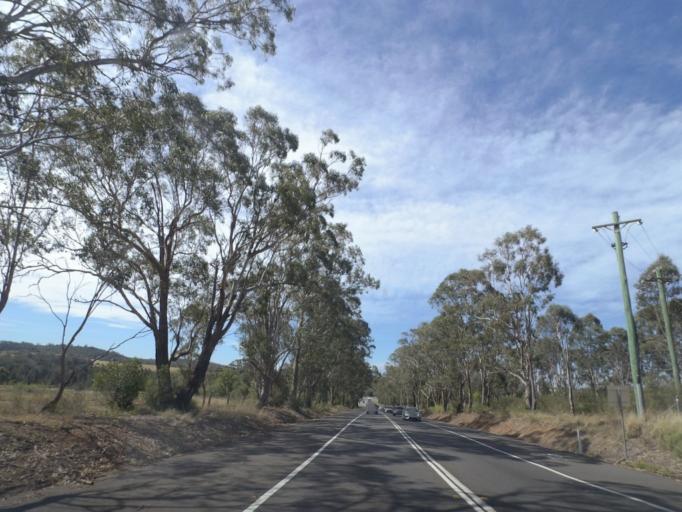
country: AU
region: New South Wales
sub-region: Campbelltown Municipality
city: Denham Court
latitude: -34.0114
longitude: 150.8374
